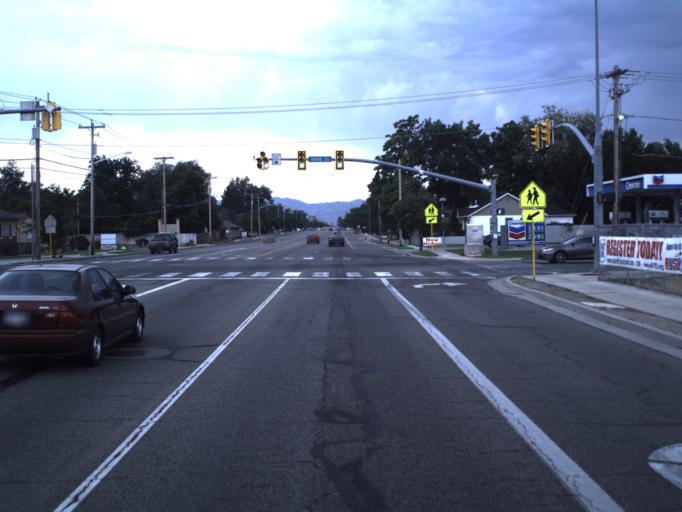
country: US
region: Utah
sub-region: Salt Lake County
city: Sandy City
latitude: 40.6063
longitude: -111.8723
